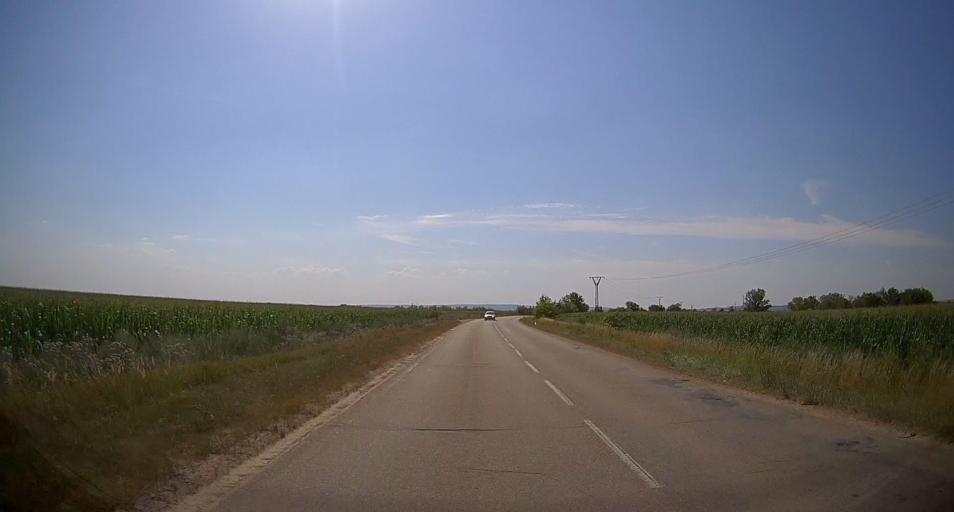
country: CZ
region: South Moravian
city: Hrusovany u Brna
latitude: 49.0478
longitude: 16.5560
